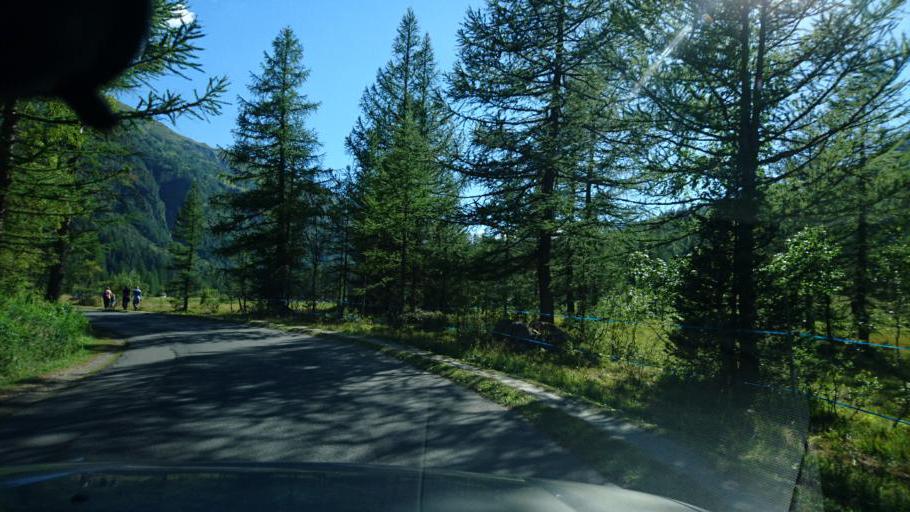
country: IT
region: Aosta Valley
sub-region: Valle d'Aosta
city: Courmayeur
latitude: 45.8483
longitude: 7.0158
